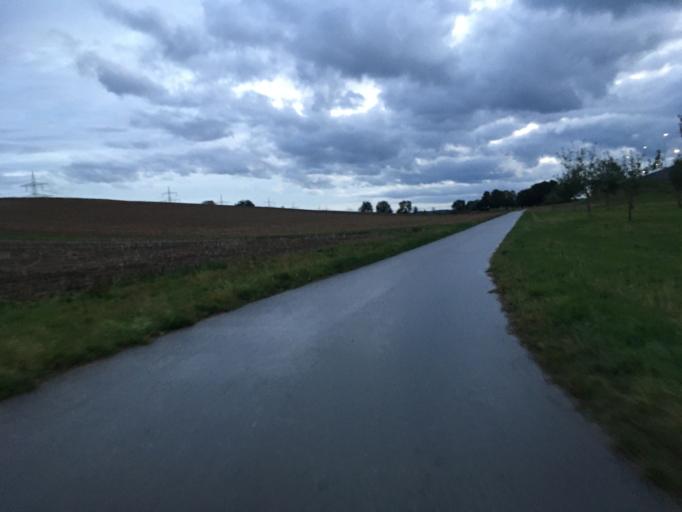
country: DE
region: Baden-Wuerttemberg
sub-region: Regierungsbezirk Stuttgart
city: Untereisesheim
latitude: 49.1784
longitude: 9.1744
